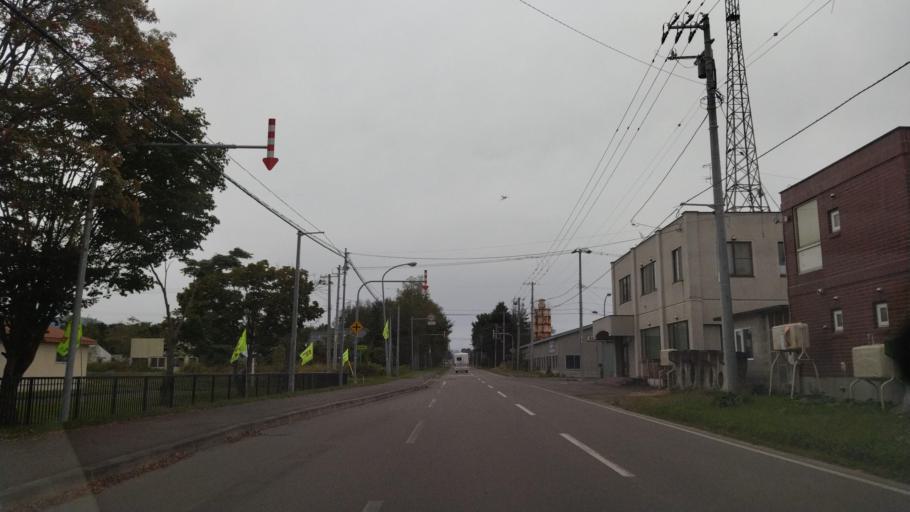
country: JP
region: Hokkaido
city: Otofuke
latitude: 43.2260
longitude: 143.2795
